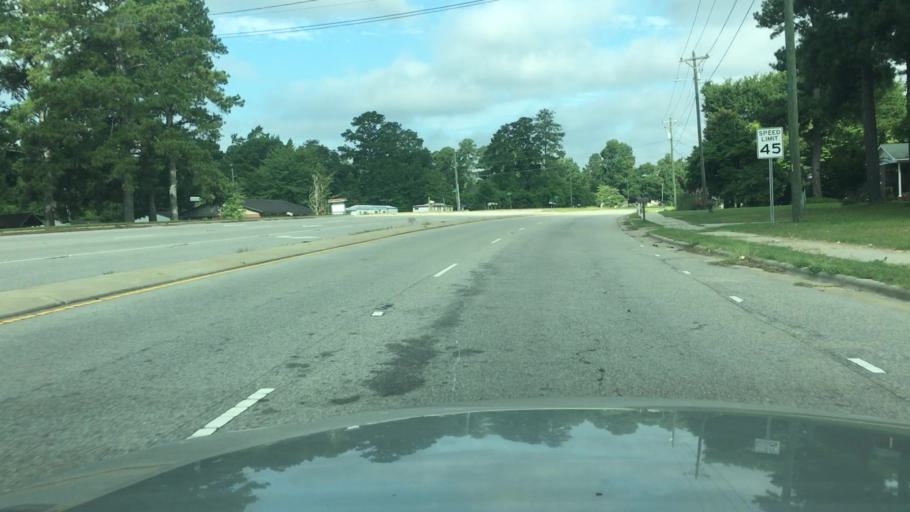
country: US
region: North Carolina
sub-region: Cumberland County
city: Hope Mills
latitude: 34.9916
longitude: -78.9610
